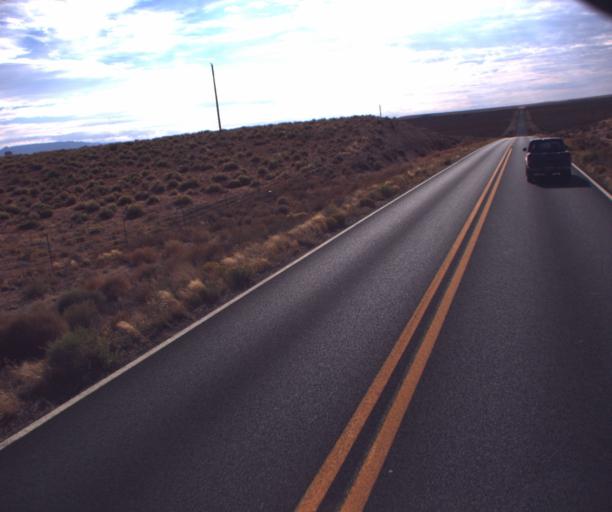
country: US
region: Arizona
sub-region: Apache County
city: Many Farms
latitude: 36.5991
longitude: -109.5684
